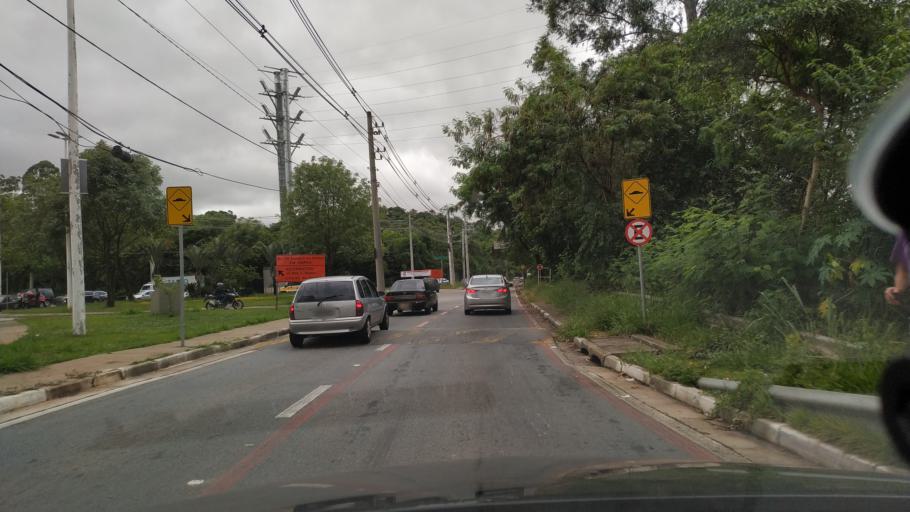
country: BR
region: Sao Paulo
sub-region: Barueri
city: Barueri
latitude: -23.4882
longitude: -46.8698
